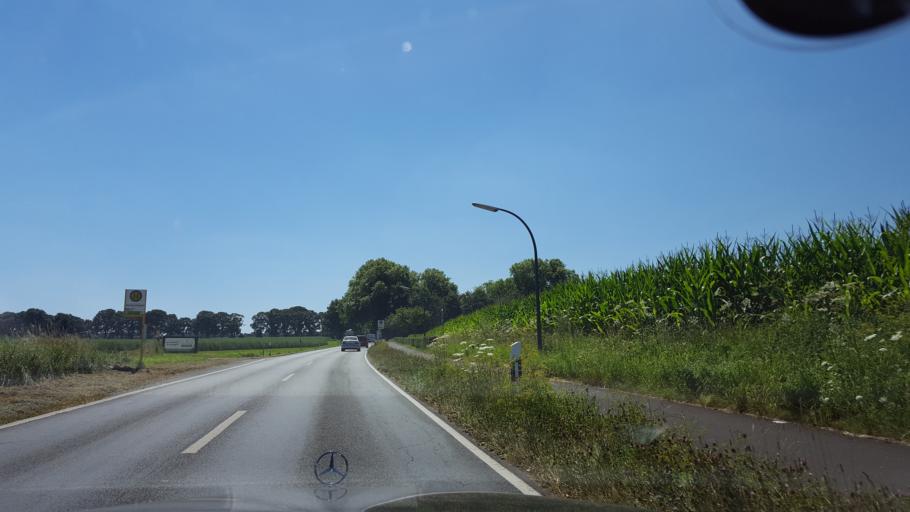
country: DE
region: North Rhine-Westphalia
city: Herten
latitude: 51.6358
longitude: 7.1557
